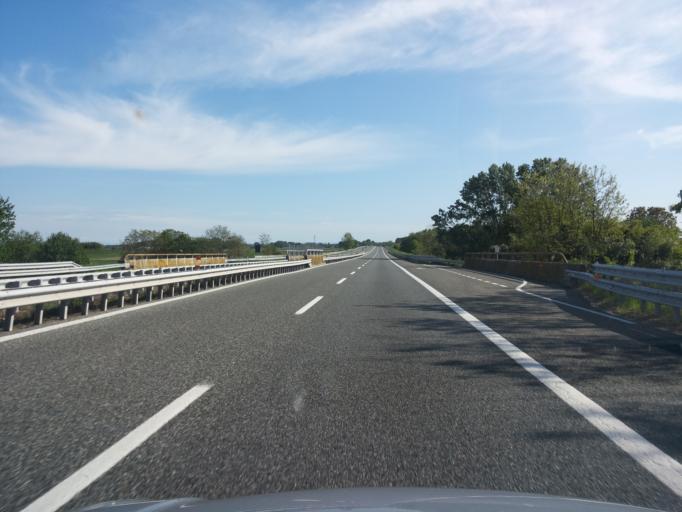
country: IT
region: Piedmont
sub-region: Provincia di Novara
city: Sillavengo
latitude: 45.5265
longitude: 8.4318
